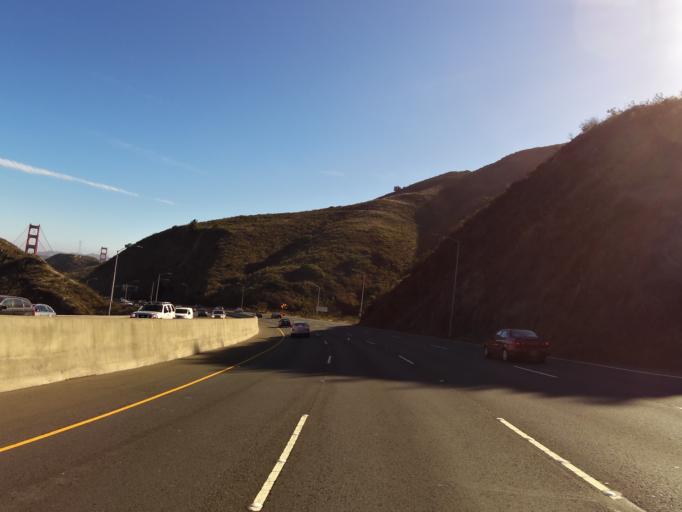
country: US
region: California
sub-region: Marin County
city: Sausalito
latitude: 37.8405
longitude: -122.4869
